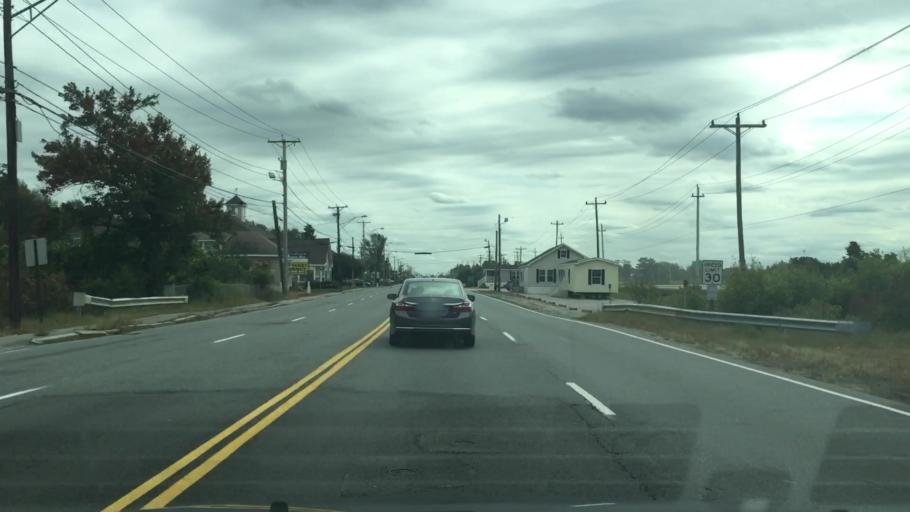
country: US
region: New Hampshire
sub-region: Rockingham County
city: Salem
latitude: 42.7744
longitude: -71.2242
